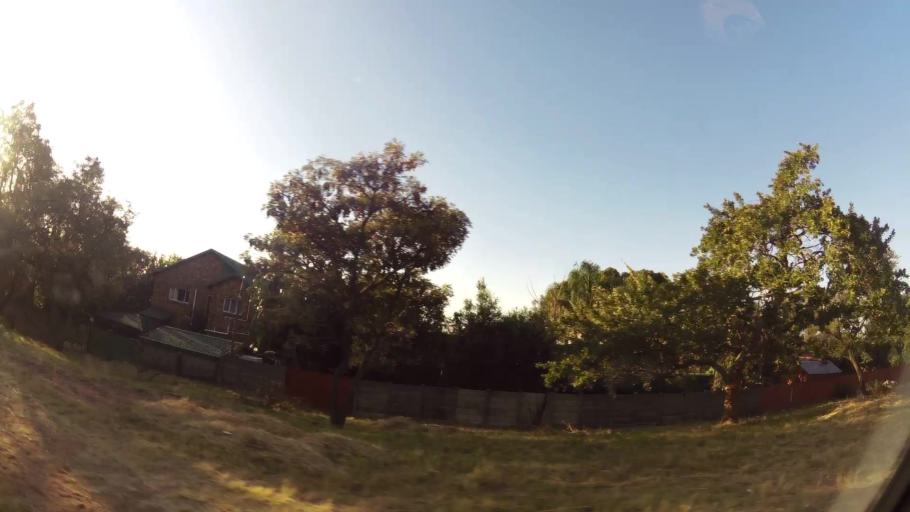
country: ZA
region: North-West
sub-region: Bojanala Platinum District Municipality
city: Rustenburg
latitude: -25.7020
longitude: 27.2245
